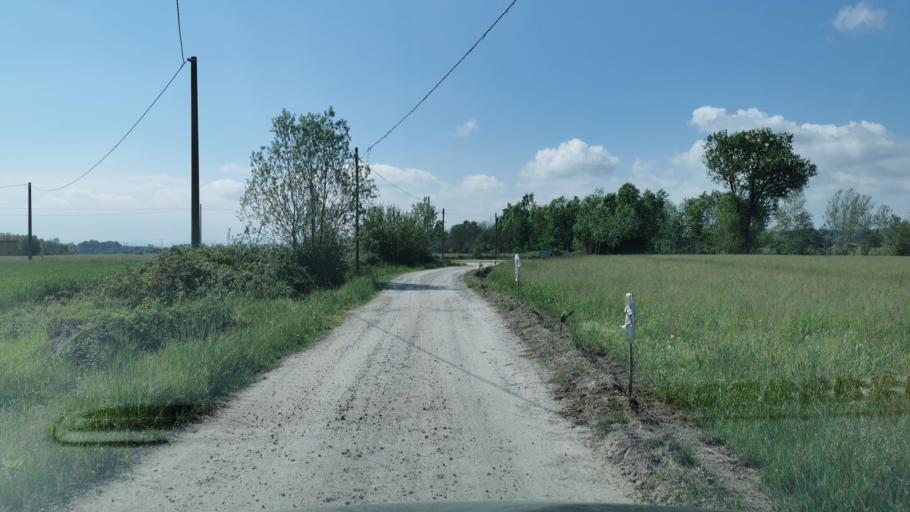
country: IT
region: Piedmont
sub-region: Provincia di Torino
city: Rivarossa
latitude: 45.2807
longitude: 7.7226
